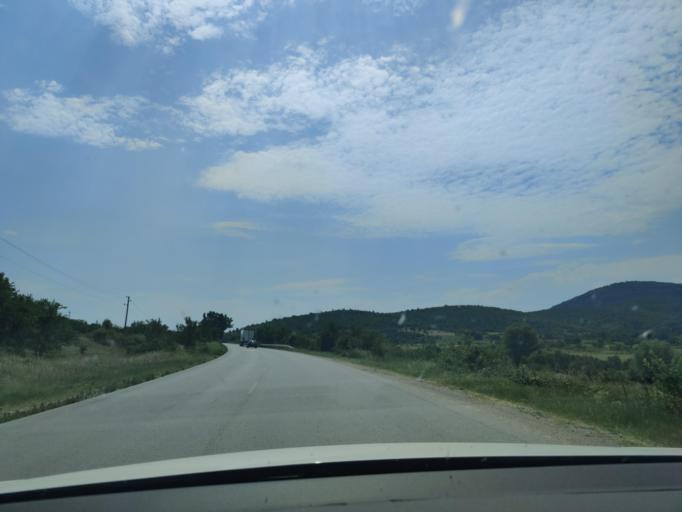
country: BG
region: Montana
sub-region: Obshtina Chiprovtsi
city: Chiprovtsi
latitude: 43.5128
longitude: 22.9792
